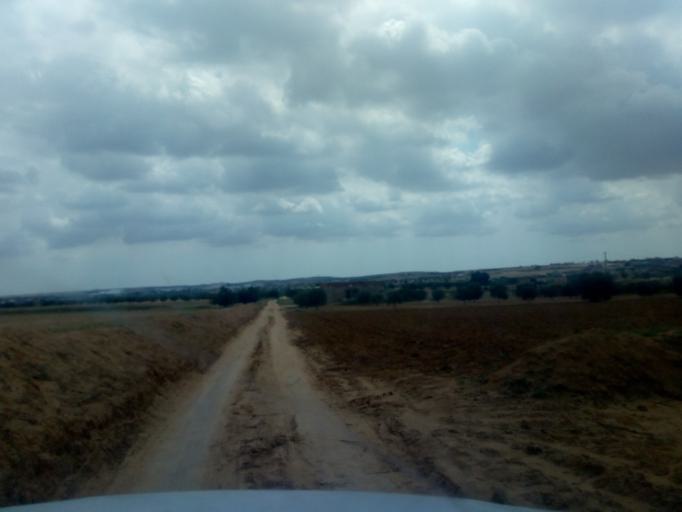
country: TN
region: Safaqis
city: Sfax
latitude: 34.7452
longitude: 10.4904
